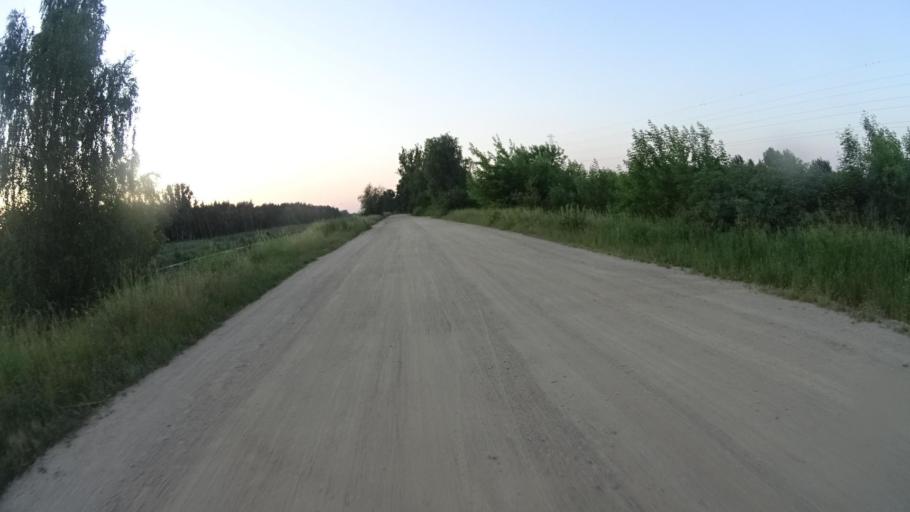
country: PL
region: Masovian Voivodeship
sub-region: Powiat legionowski
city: Stanislawow Pierwszy
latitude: 52.3463
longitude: 21.0340
